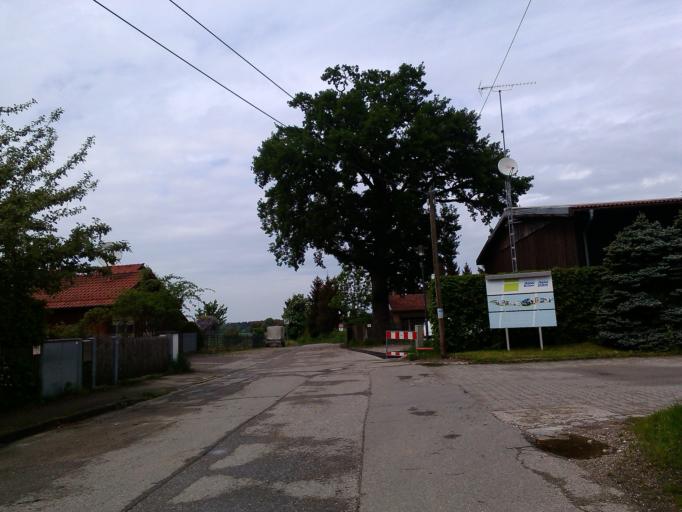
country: DE
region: Bavaria
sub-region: Upper Bavaria
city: Gauting
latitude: 48.0588
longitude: 11.4012
